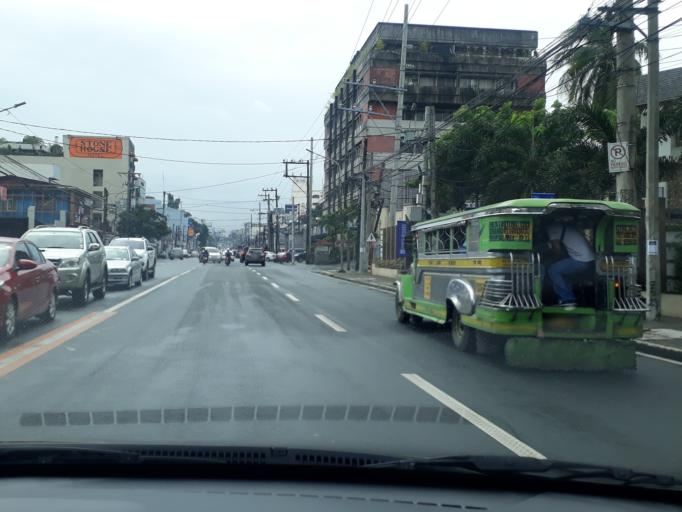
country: PH
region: Calabarzon
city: Del Monte
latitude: 14.6241
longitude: 121.0333
